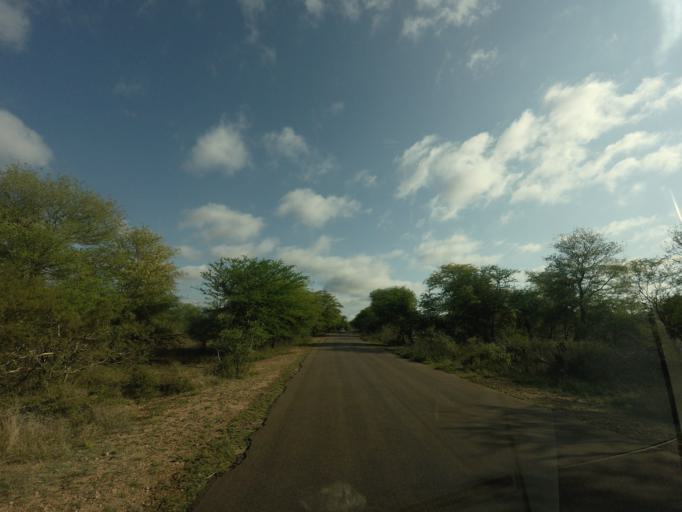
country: ZA
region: Mpumalanga
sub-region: Ehlanzeni District
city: Komatipoort
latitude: -25.2337
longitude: 31.8508
